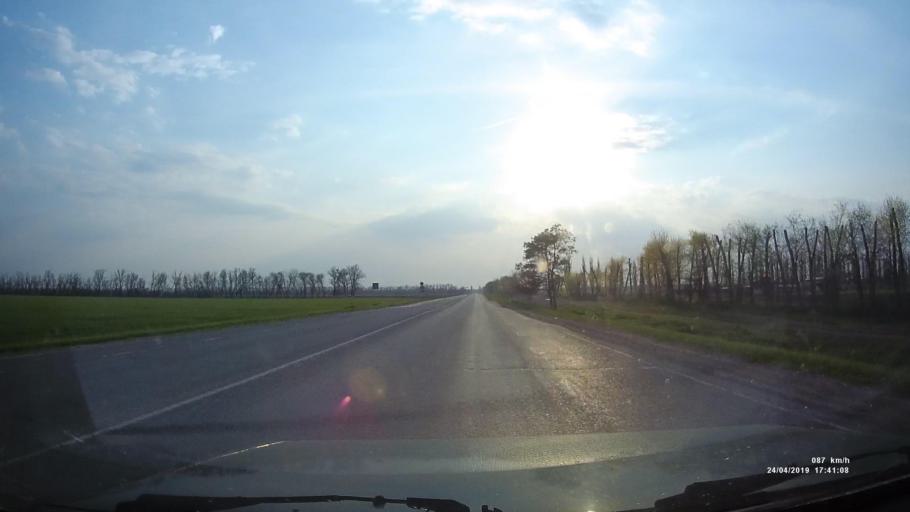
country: RU
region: Rostov
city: Tselina
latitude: 46.5310
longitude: 40.9770
